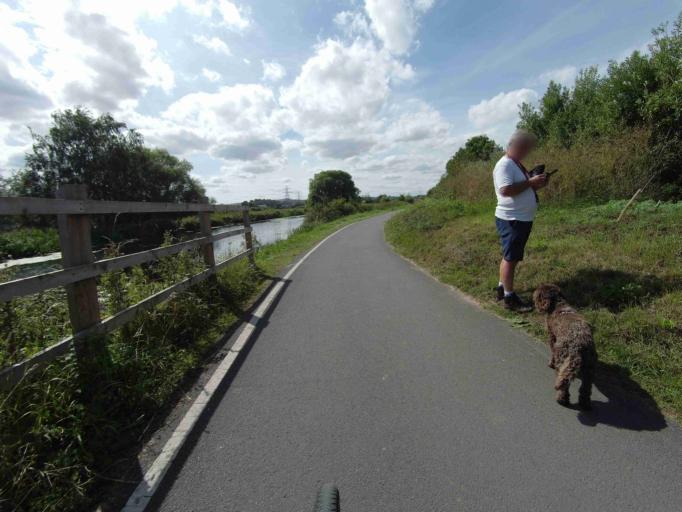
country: GB
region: England
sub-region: Devon
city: Exminster
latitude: 50.6953
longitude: -3.5034
